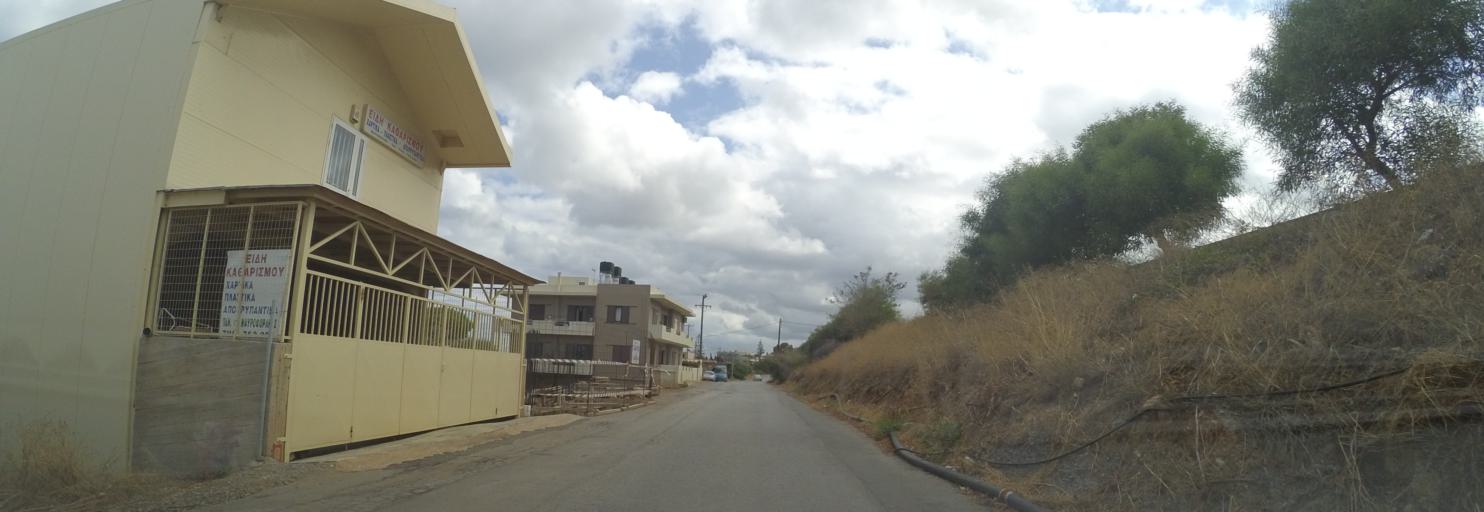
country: GR
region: Crete
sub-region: Nomos Irakleiou
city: Gournes
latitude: 35.3288
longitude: 25.2689
